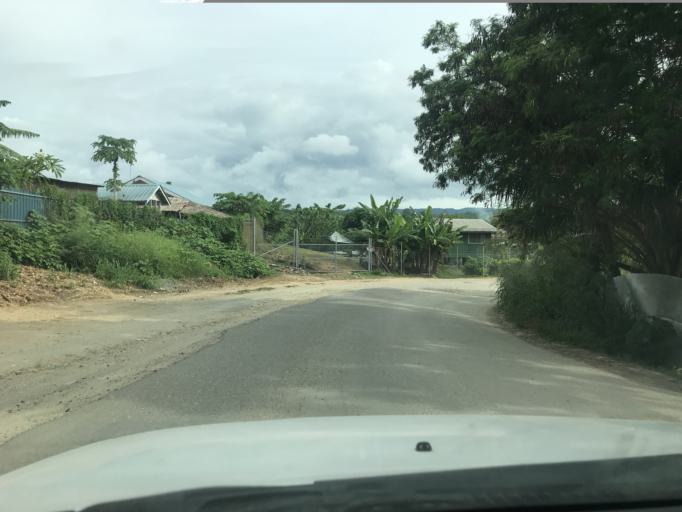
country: SB
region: Guadalcanal
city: Honiara
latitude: -9.4365
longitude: 159.9451
